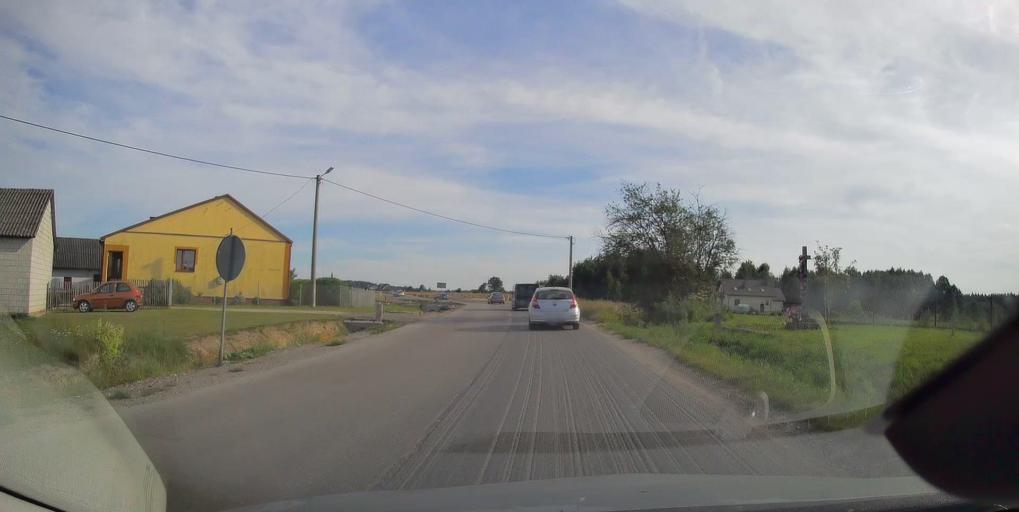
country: PL
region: Swietokrzyskie
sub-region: Powiat kielecki
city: Lopuszno
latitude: 50.9680
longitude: 20.2453
